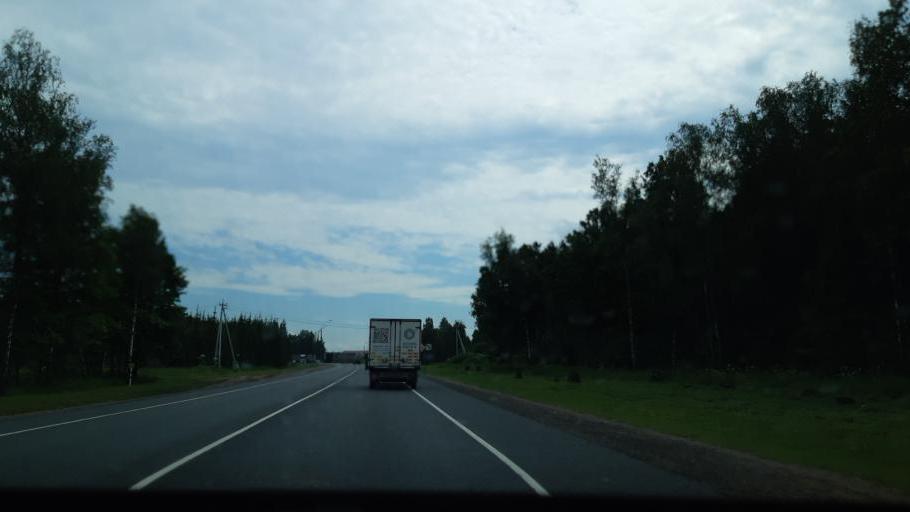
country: RU
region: Moskovskaya
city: Dorokhovo
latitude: 55.4342
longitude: 36.3518
